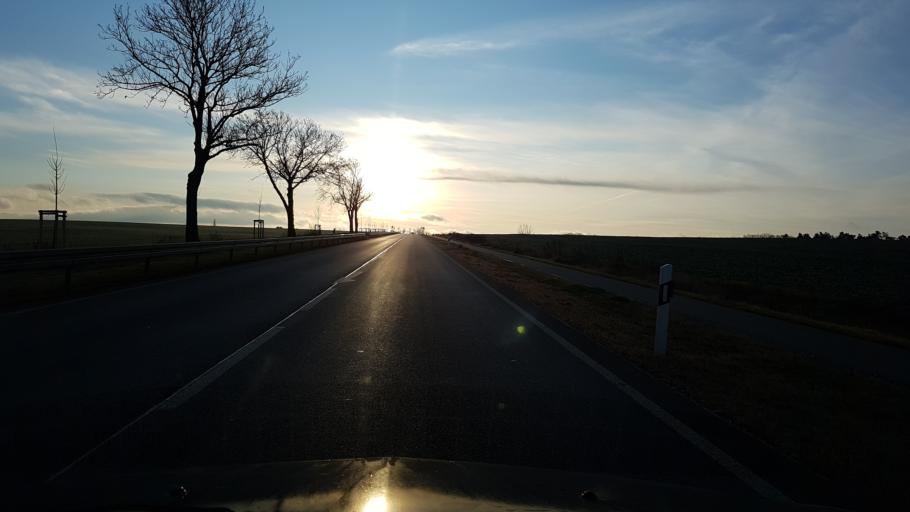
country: DE
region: Saxony
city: Radibor
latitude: 51.2334
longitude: 14.3740
